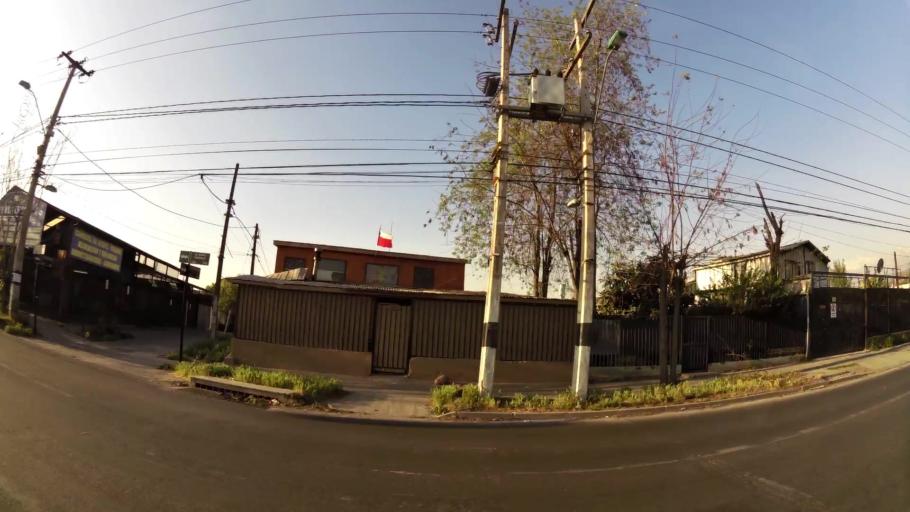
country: CL
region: Santiago Metropolitan
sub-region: Provincia de Santiago
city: La Pintana
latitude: -33.5457
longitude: -70.6183
